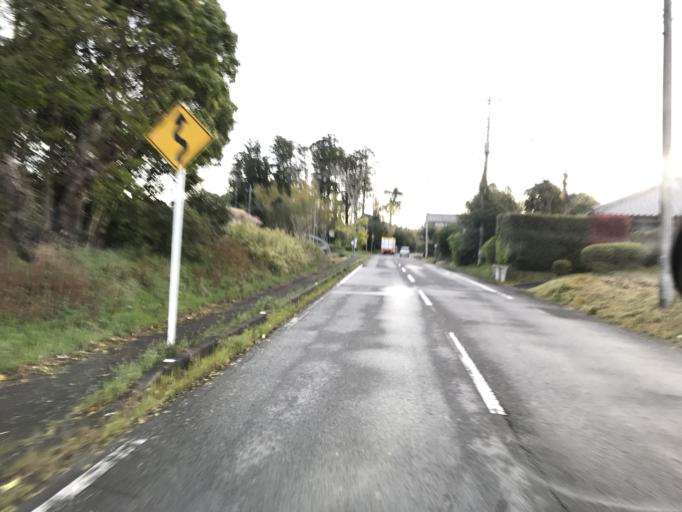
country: JP
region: Chiba
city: Yokaichiba
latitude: 35.7493
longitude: 140.5296
